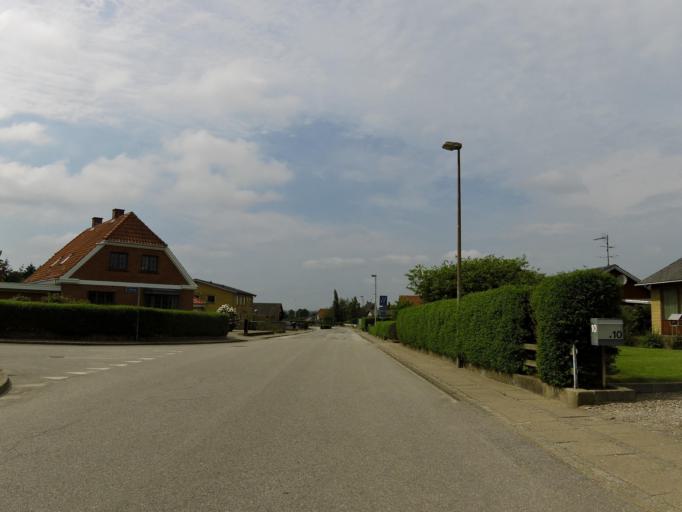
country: DK
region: South Denmark
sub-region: Haderslev Kommune
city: Vojens
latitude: 55.2700
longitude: 9.1854
